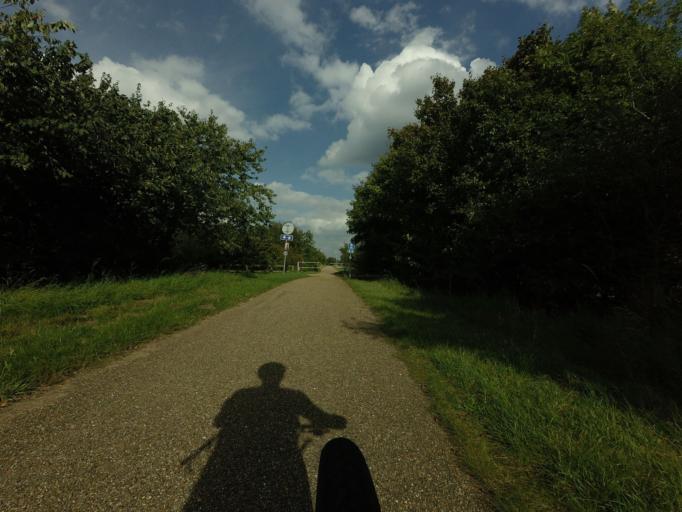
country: DK
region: Central Jutland
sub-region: Herning Kommune
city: Sunds
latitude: 56.2329
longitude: 9.0841
